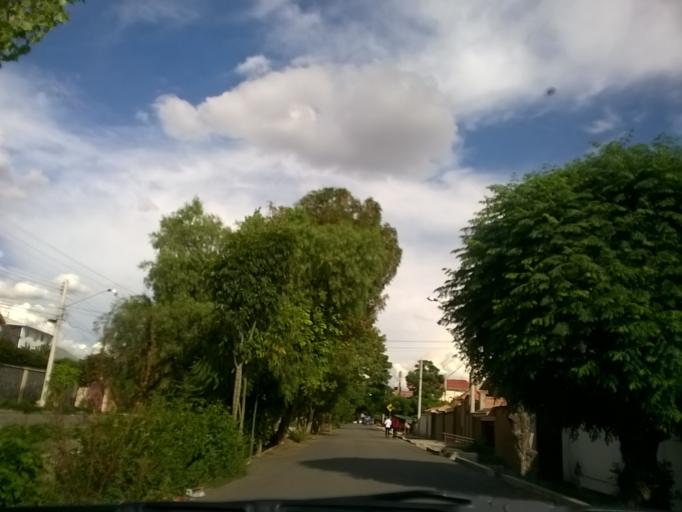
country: BO
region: Cochabamba
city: Cochabamba
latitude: -17.3648
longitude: -66.1826
